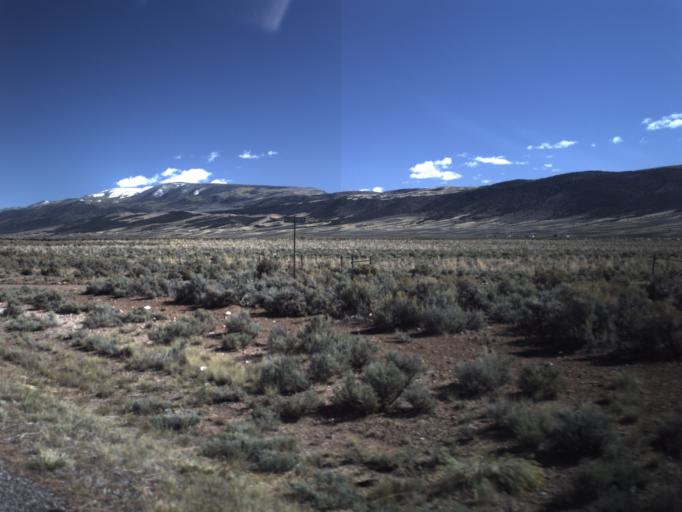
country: US
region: Utah
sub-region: Wayne County
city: Loa
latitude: 38.4163
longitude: -111.9246
